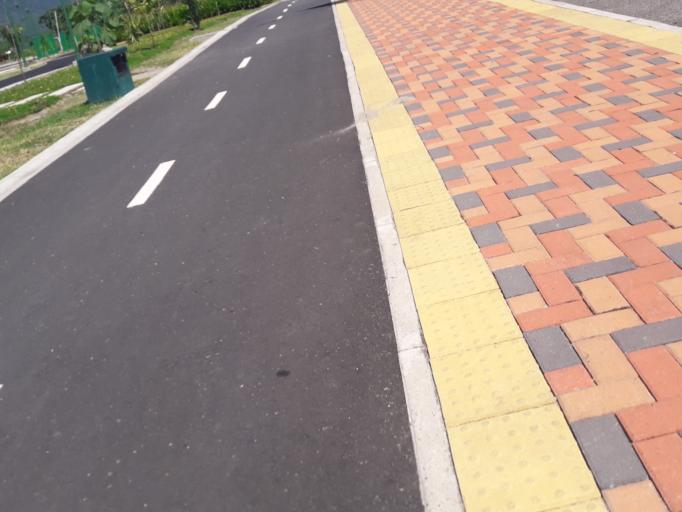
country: EC
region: Napo
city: Tena
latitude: -0.9873
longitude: -77.8235
